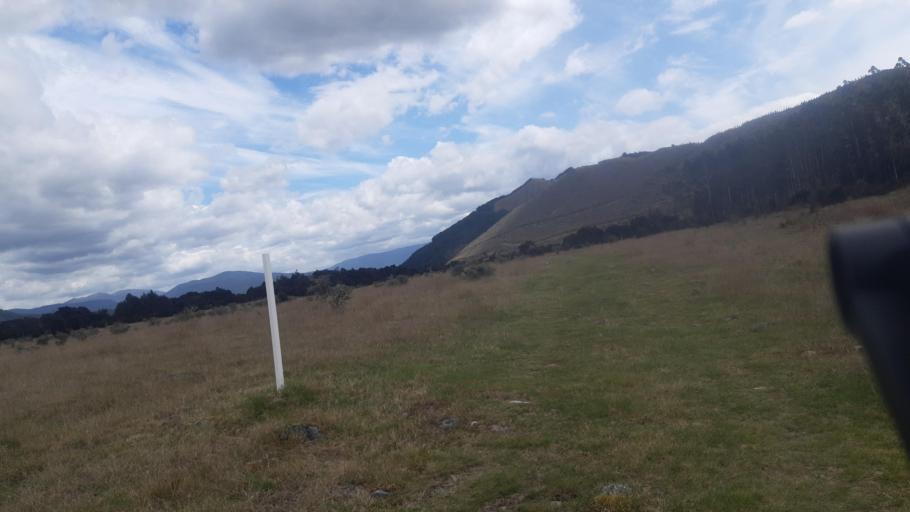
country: NZ
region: Tasman
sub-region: Tasman District
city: Wakefield
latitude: -41.7721
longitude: 172.8001
